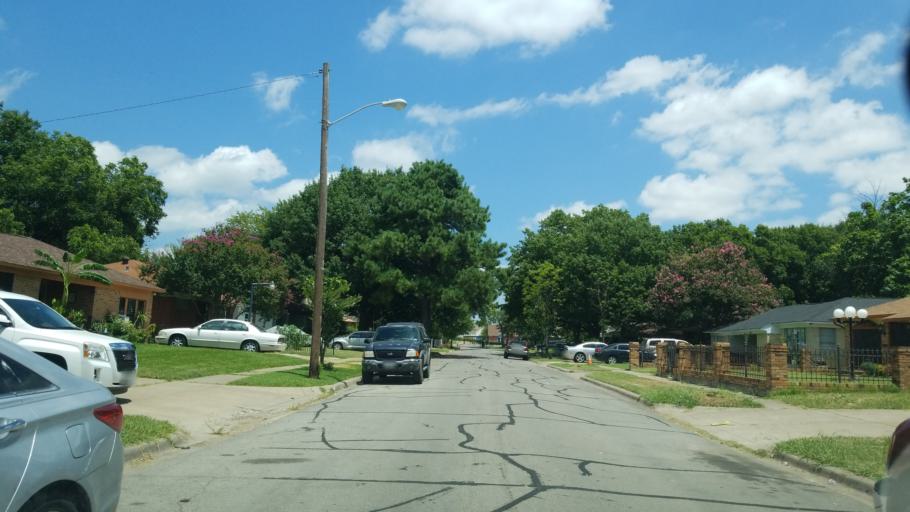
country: US
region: Texas
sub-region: Dallas County
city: Balch Springs
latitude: 32.7433
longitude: -96.6987
